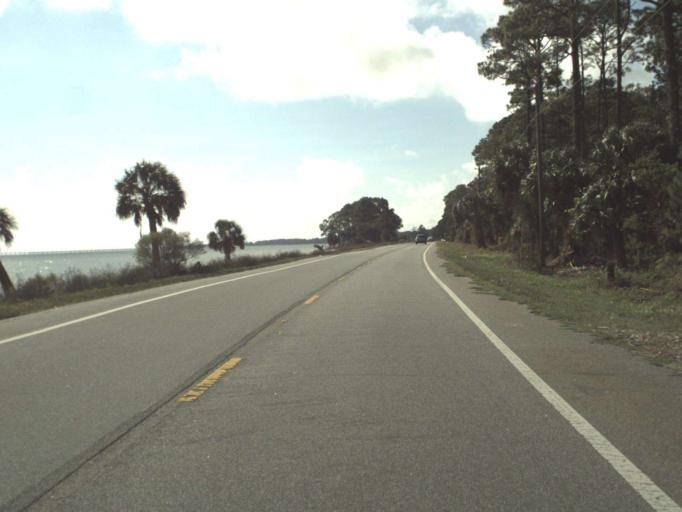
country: US
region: Florida
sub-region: Franklin County
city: Eastpoint
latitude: 29.7513
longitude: -84.8467
